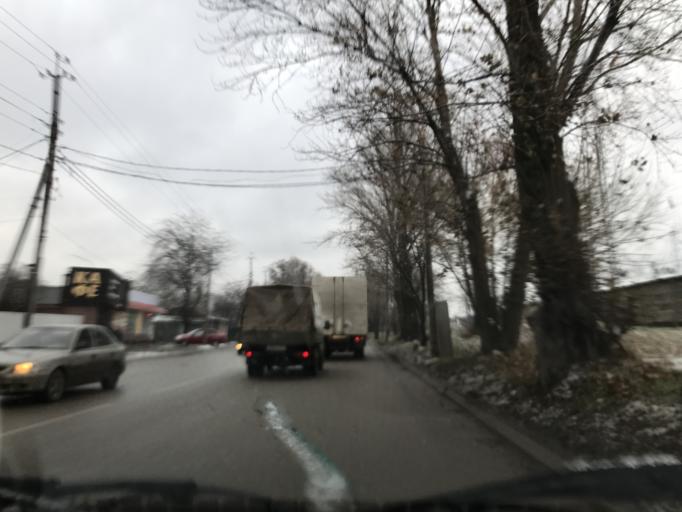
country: RU
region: Rostov
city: Rostov-na-Donu
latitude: 47.2440
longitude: 39.7397
